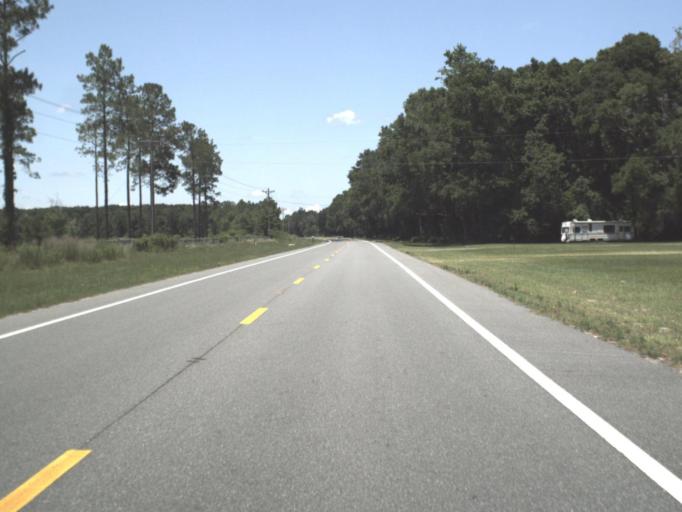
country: US
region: Florida
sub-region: Lafayette County
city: Mayo
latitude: 29.9355
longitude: -82.9490
